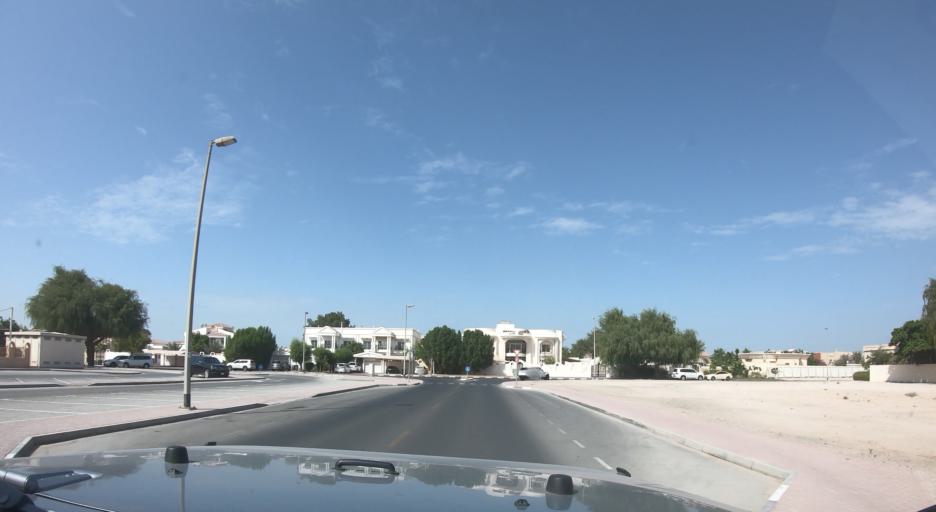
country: AE
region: Dubai
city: Dubai
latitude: 25.1564
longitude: 55.2226
